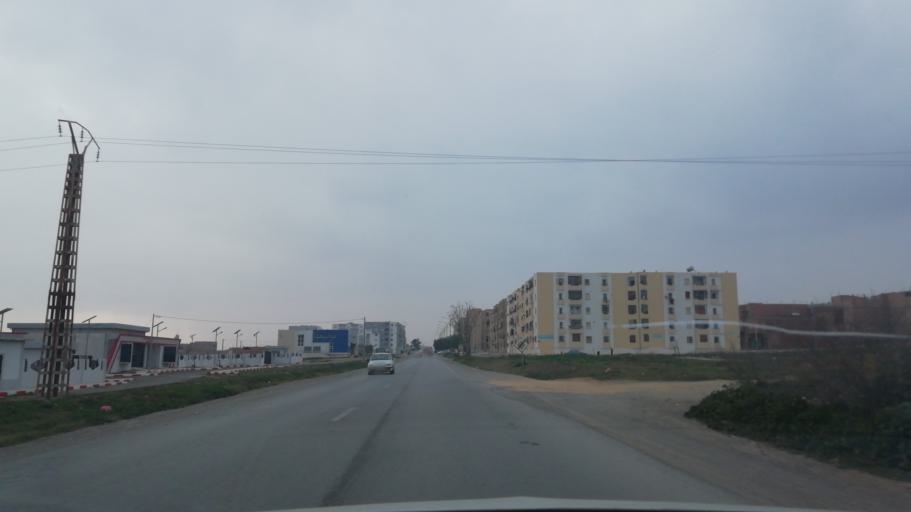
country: DZ
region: Sidi Bel Abbes
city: Sfizef
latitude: 35.2420
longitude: -0.2255
